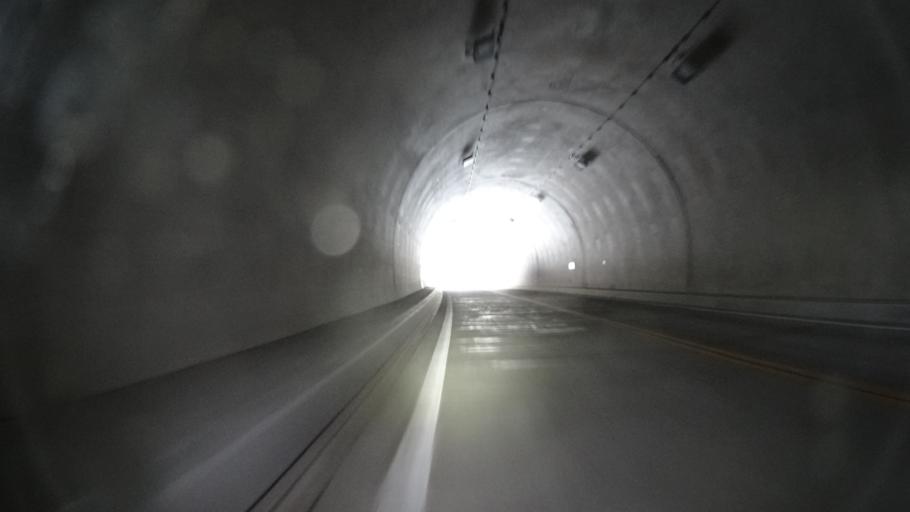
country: JP
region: Yamanashi
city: Enzan
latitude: 35.8029
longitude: 138.8648
